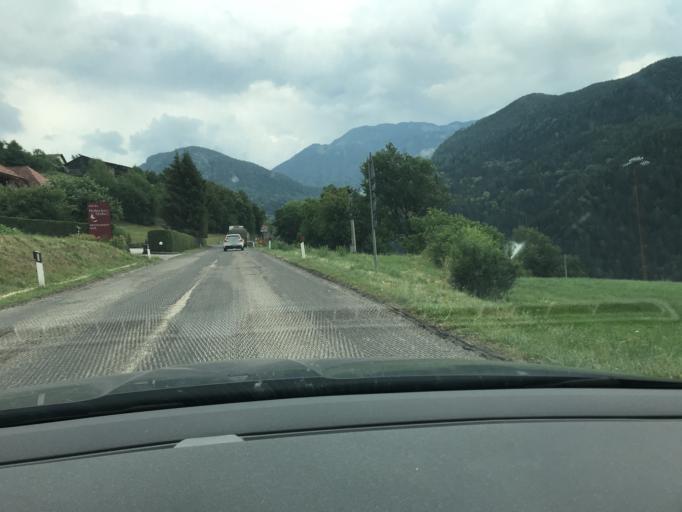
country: IT
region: Trentino-Alto Adige
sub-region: Bolzano
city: Laion
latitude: 46.6018
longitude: 11.5613
